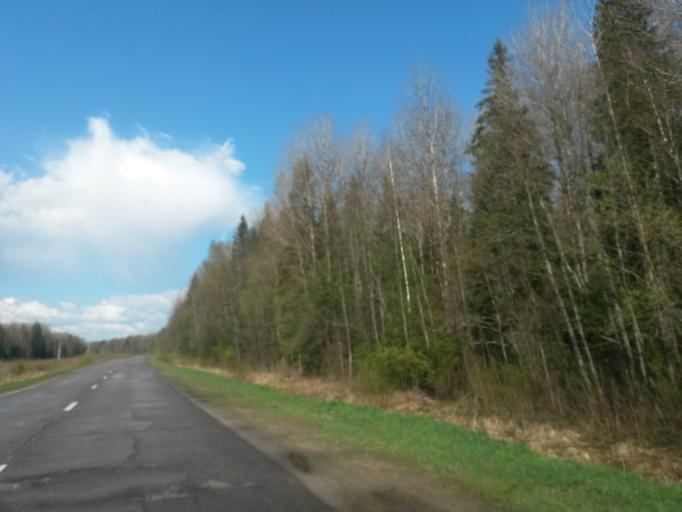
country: RU
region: Jaroslavl
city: Tutayev
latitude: 57.9509
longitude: 39.4992
